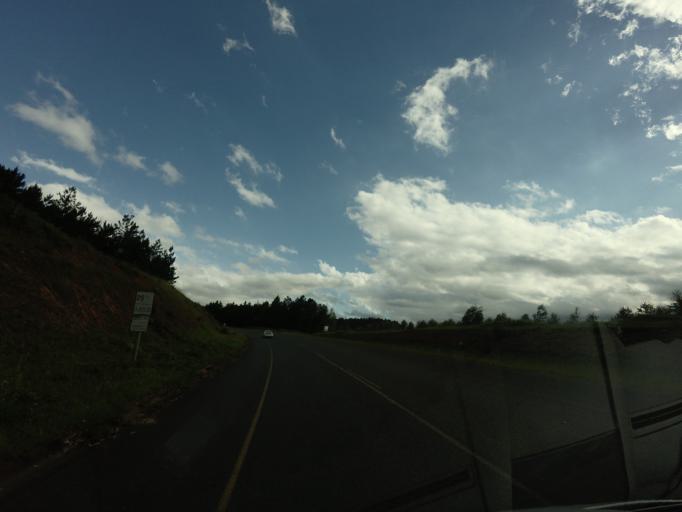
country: ZA
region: Mpumalanga
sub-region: Ehlanzeni District
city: Graksop
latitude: -24.9725
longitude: 30.9417
